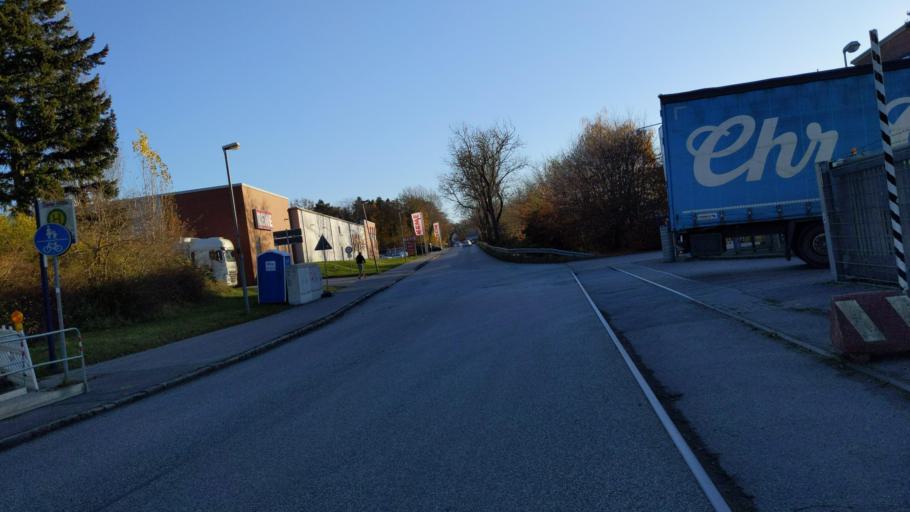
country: DE
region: Schleswig-Holstein
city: Bad Schwartau
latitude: 53.8926
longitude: 10.7073
